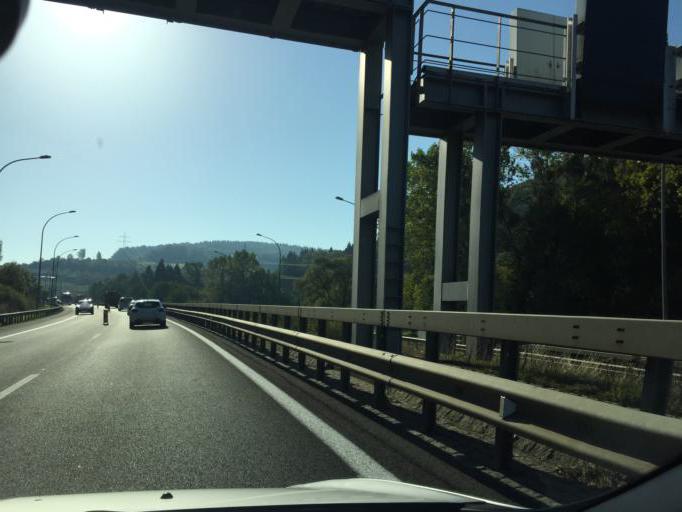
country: LU
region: Luxembourg
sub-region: Canton de Mersch
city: Mersch
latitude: 49.7351
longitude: 6.0993
